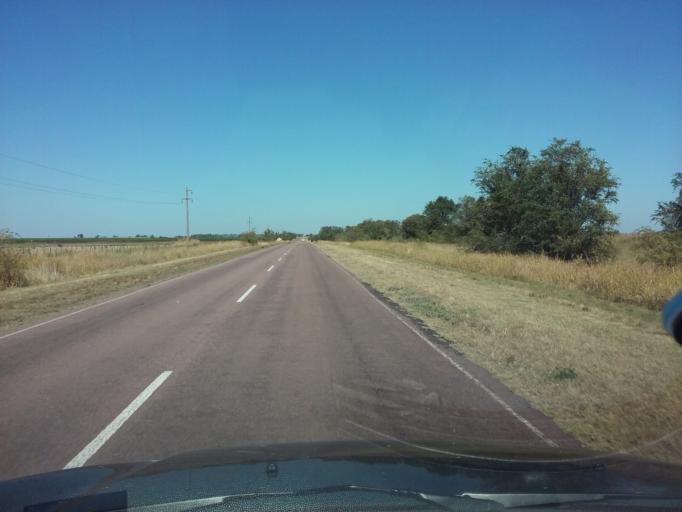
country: AR
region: La Pampa
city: Colonia Baron
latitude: -36.2572
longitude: -63.9428
